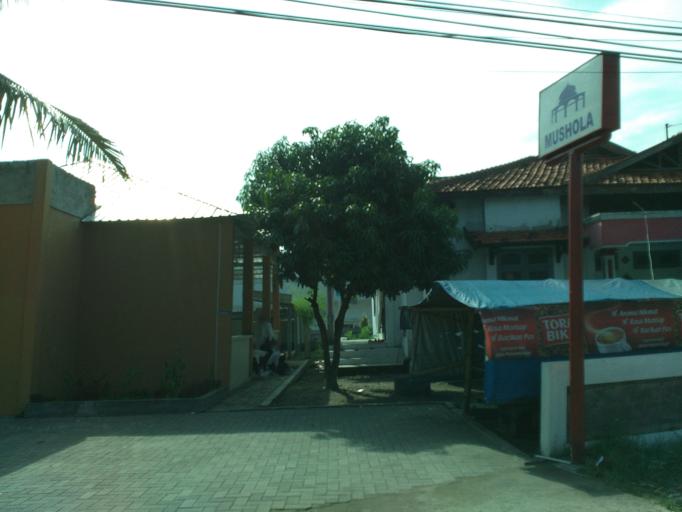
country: ID
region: Central Java
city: Delanggu
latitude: -7.6385
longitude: 110.6912
